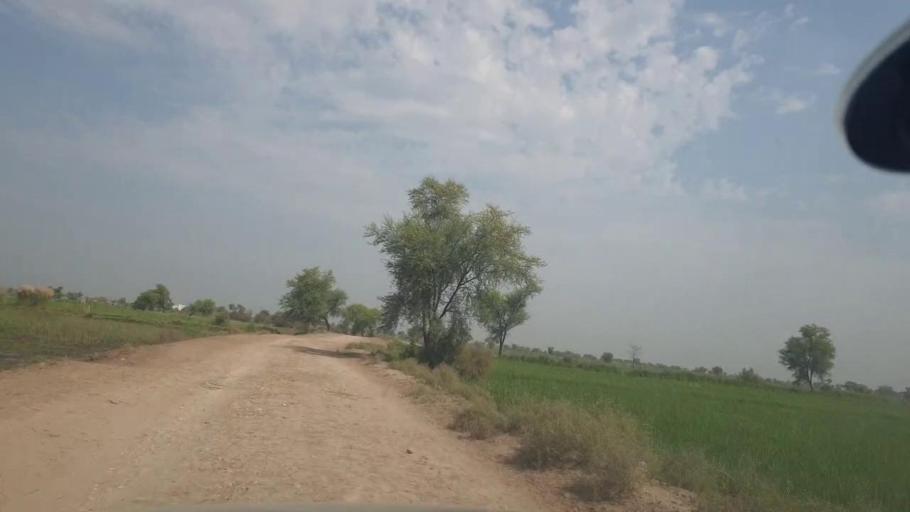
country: PK
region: Balochistan
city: Mehrabpur
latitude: 28.1223
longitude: 68.0907
